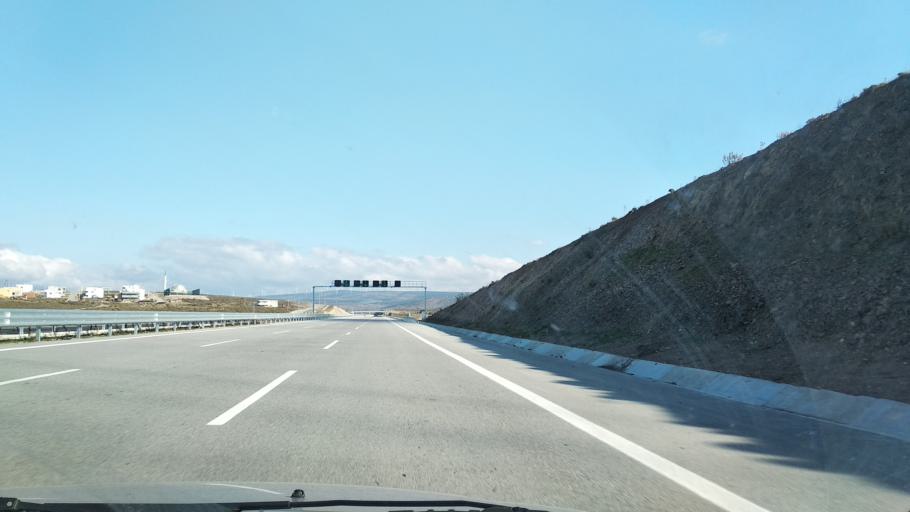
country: TR
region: Izmir
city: Yenisakran
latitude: 38.8537
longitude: 27.0578
